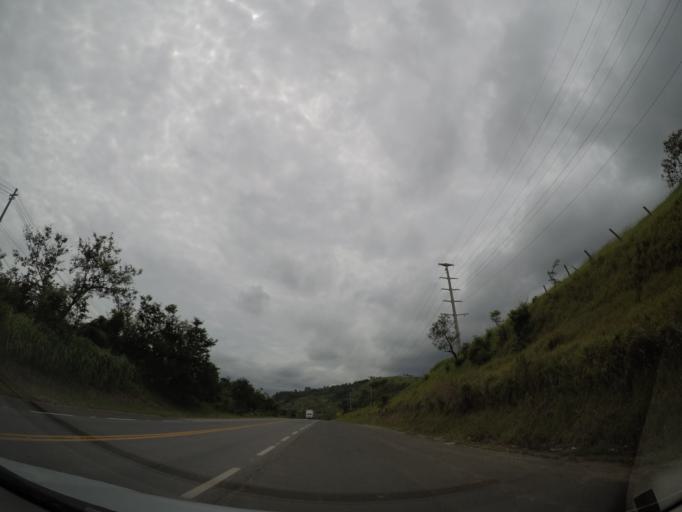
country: BR
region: Sao Paulo
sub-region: Vinhedo
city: Vinhedo
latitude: -23.0598
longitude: -47.0292
